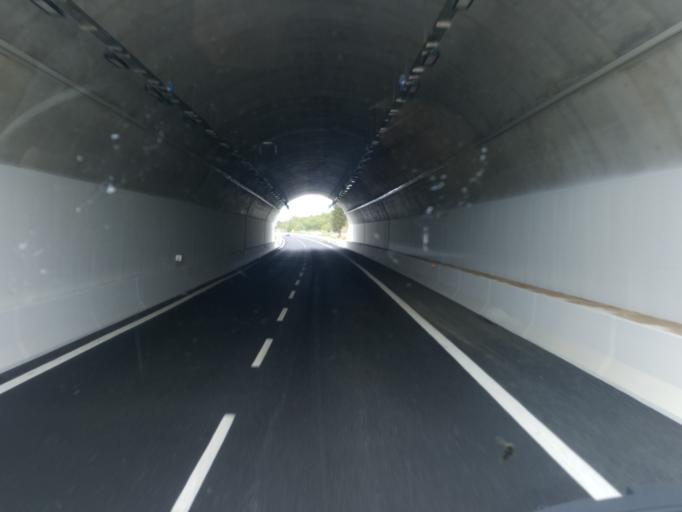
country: IT
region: Latium
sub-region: Provincia di Viterbo
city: Monte Romano
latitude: 42.2858
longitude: 11.9349
